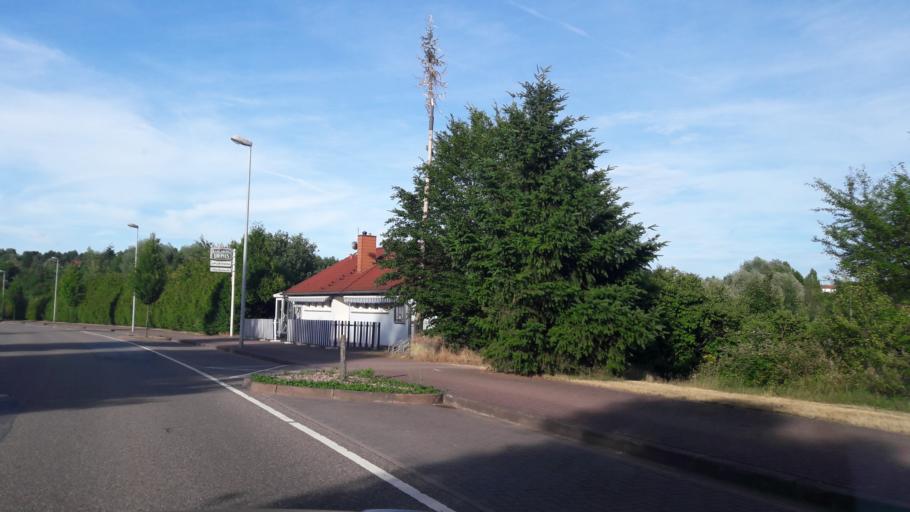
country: DE
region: Saarland
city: Bexbach
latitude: 49.3602
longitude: 7.2556
